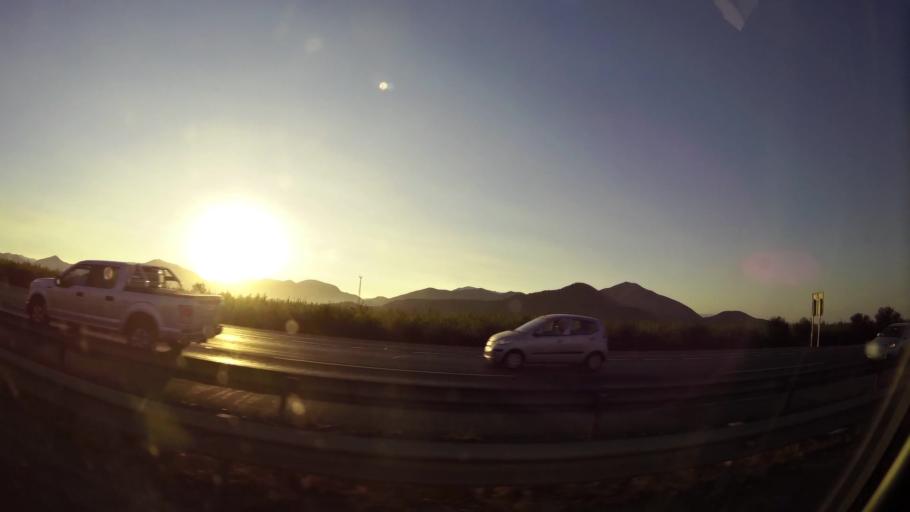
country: CL
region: Santiago Metropolitan
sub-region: Provincia de Santiago
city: Lo Prado
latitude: -33.5023
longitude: -70.7984
